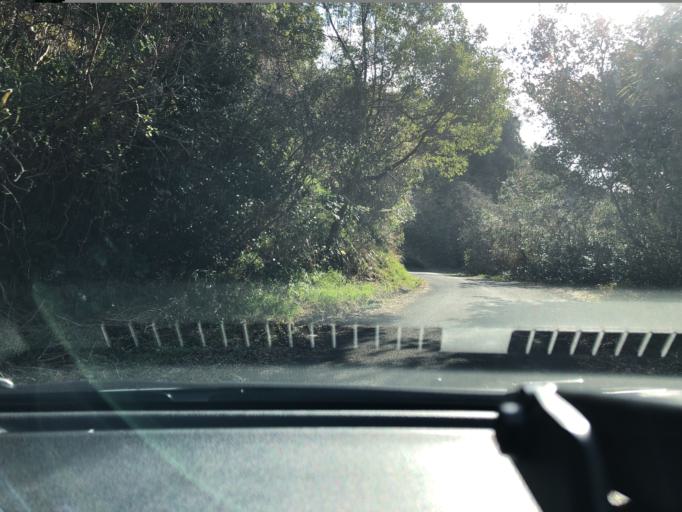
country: JP
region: Kochi
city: Sukumo
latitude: 32.9142
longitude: 132.6887
